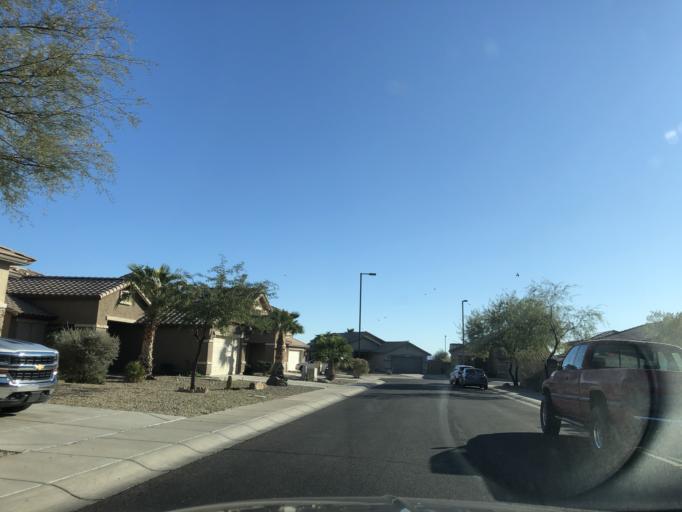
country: US
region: Arizona
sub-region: Maricopa County
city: Buckeye
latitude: 33.4272
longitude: -112.6043
